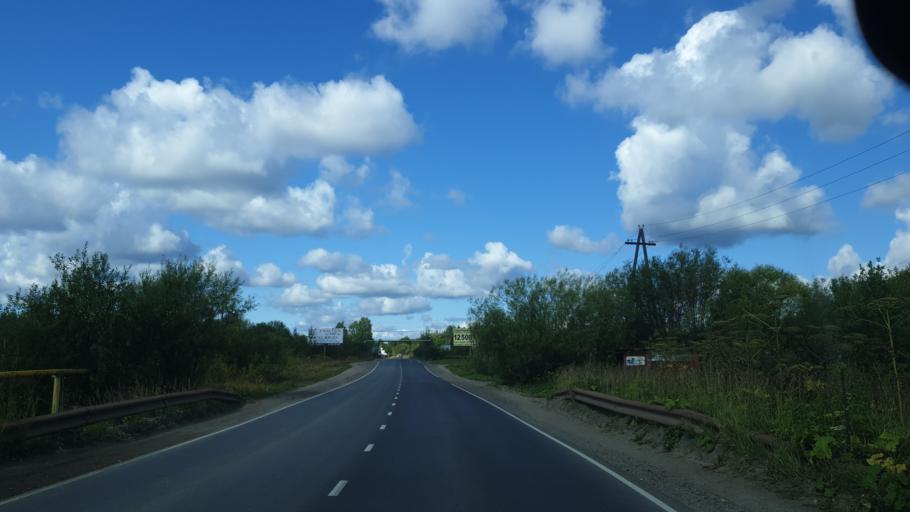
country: RU
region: Komi Republic
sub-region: Syktyvdinskiy Rayon
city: Syktyvkar
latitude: 61.6397
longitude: 50.7995
